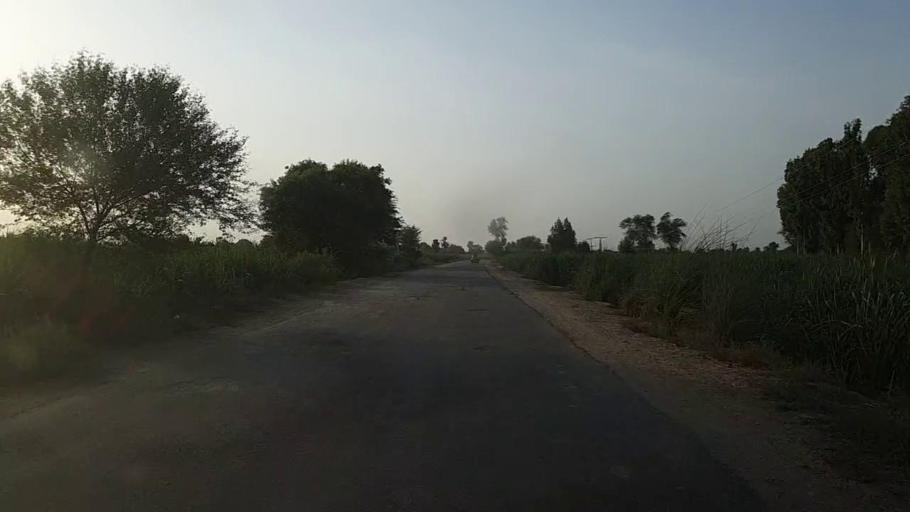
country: PK
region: Sindh
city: Ubauro
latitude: 28.1708
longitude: 69.8313
